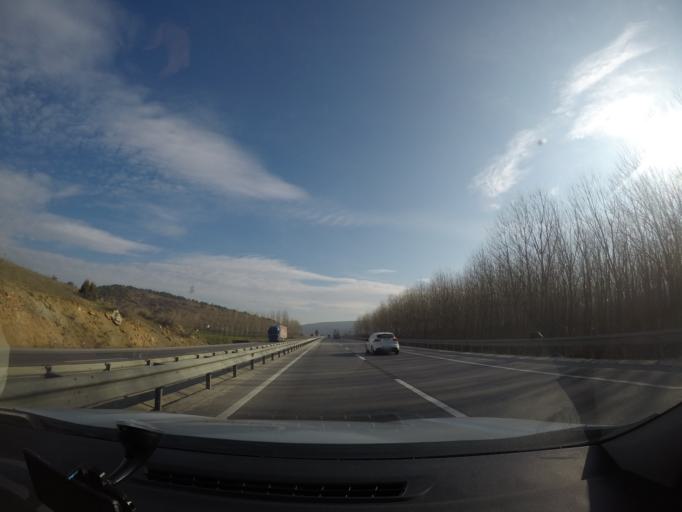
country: TR
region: Bilecik
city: Bozuyuk
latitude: 39.8957
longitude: 29.9795
